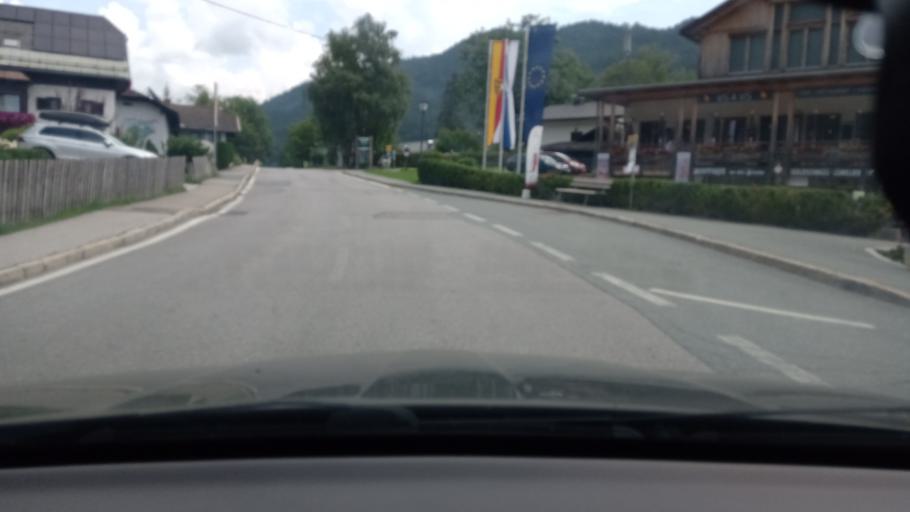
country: AT
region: Carinthia
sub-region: Politischer Bezirk Spittal an der Drau
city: Steinfeld
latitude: 46.7144
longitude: 13.2943
